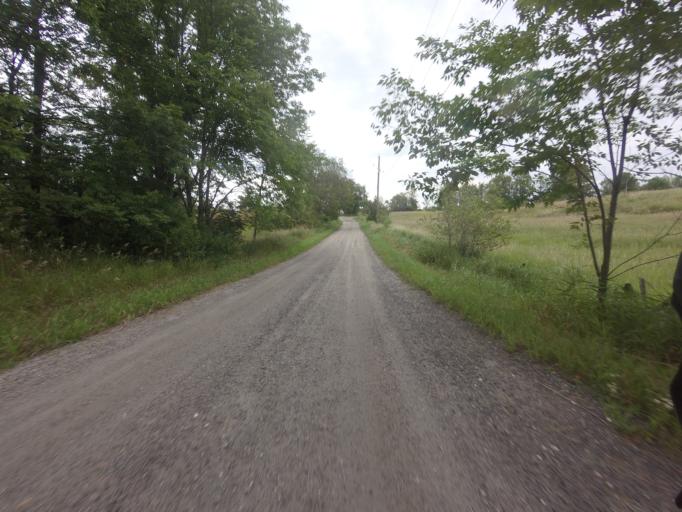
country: CA
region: Ontario
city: Perth
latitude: 45.0555
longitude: -76.3922
